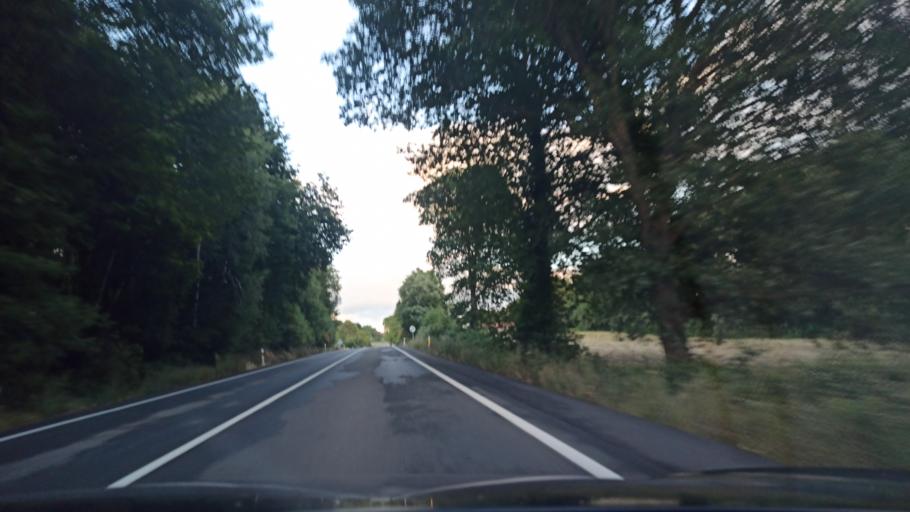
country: ES
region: Galicia
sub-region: Provincia de Lugo
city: Monterroso
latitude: 42.7812
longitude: -7.9083
